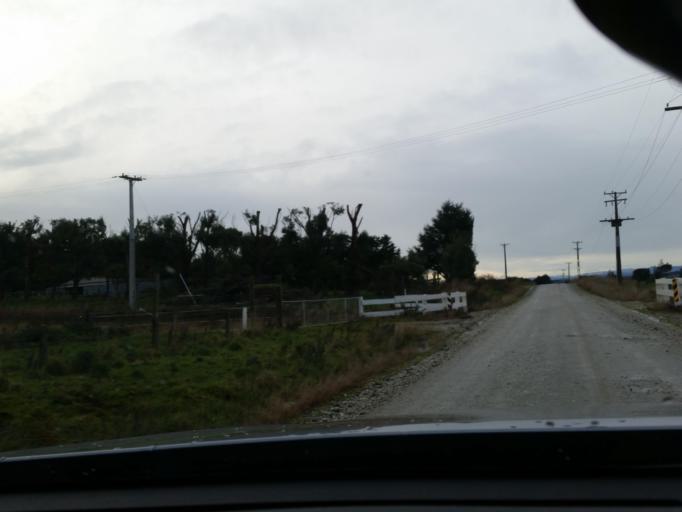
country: NZ
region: Southland
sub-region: Invercargill City
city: Invercargill
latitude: -46.4113
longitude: 168.5325
